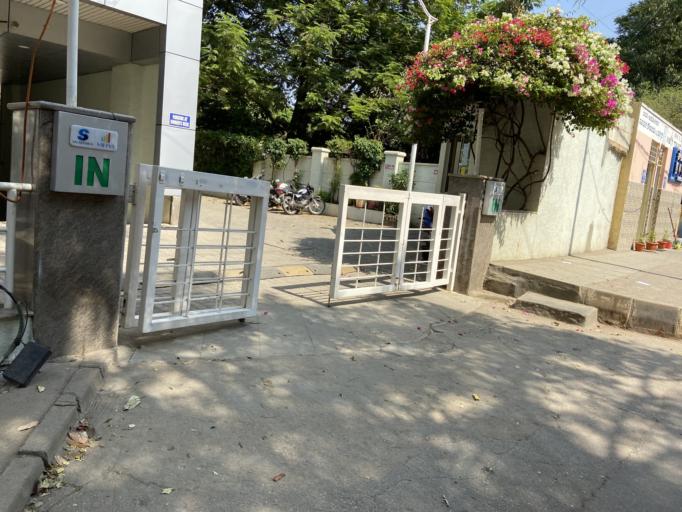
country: IN
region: Karnataka
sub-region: Bangalore Urban
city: Bangalore
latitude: 12.9738
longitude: 77.6261
